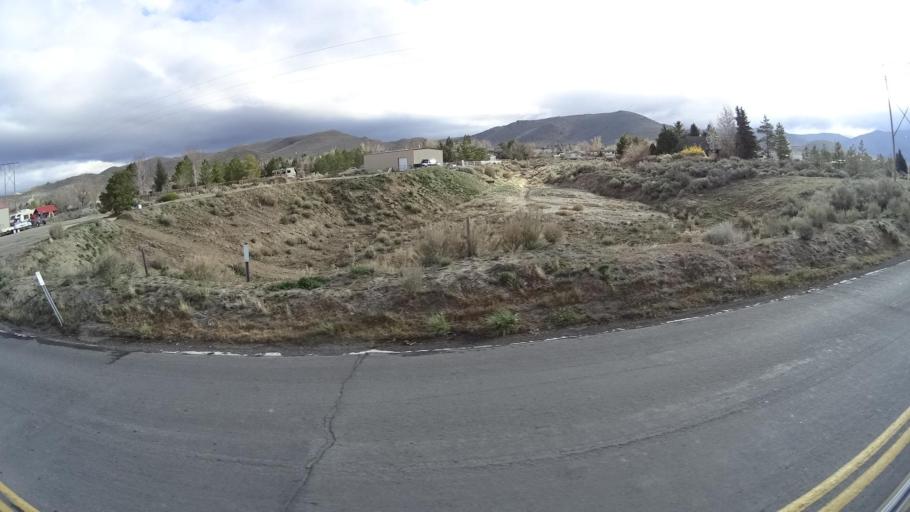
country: US
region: Nevada
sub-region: Storey County
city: Virginia City
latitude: 39.2921
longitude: -119.7714
